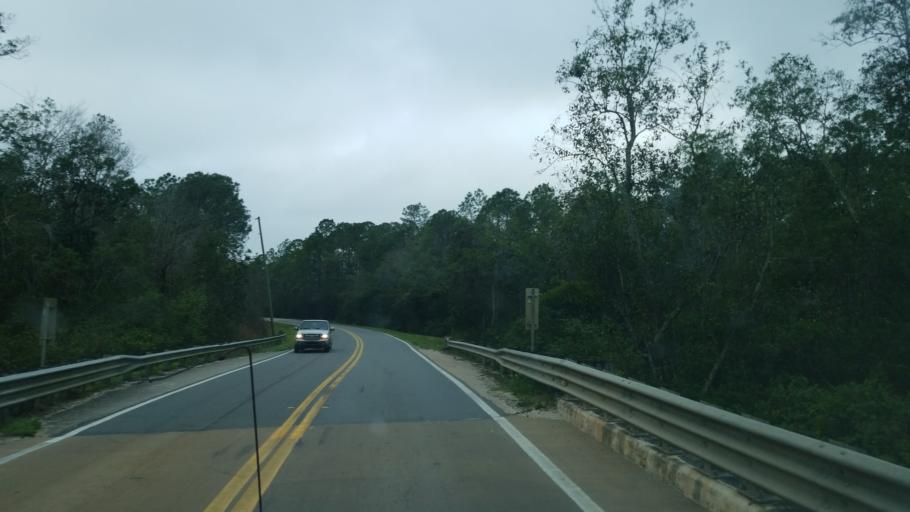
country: US
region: Florida
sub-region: Lake County
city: Four Corners
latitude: 28.2590
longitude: -81.7309
